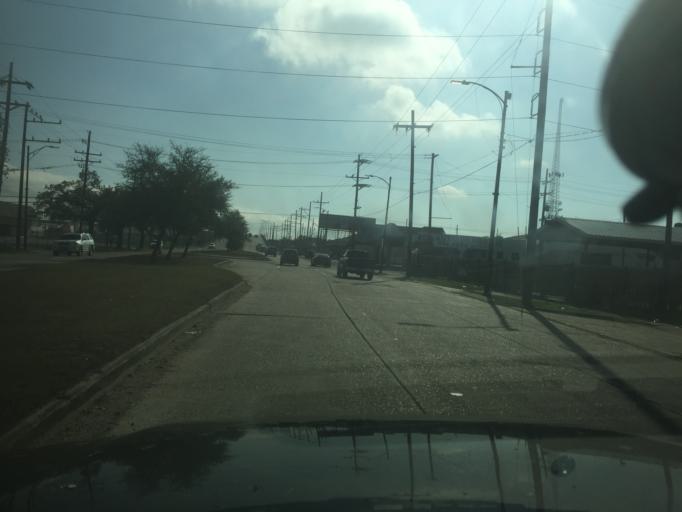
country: US
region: Louisiana
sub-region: Orleans Parish
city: New Orleans
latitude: 29.9898
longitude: -90.0494
